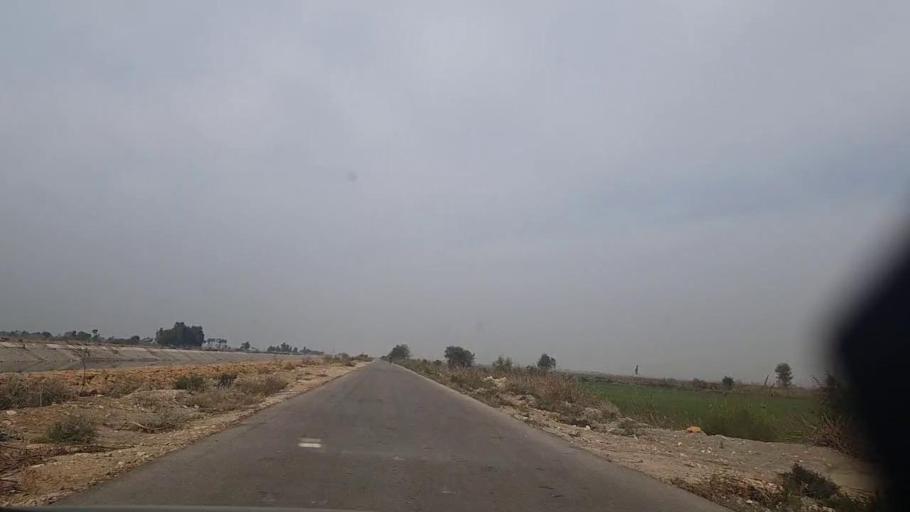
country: PK
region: Sindh
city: Sakrand
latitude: 26.2564
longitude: 68.2462
